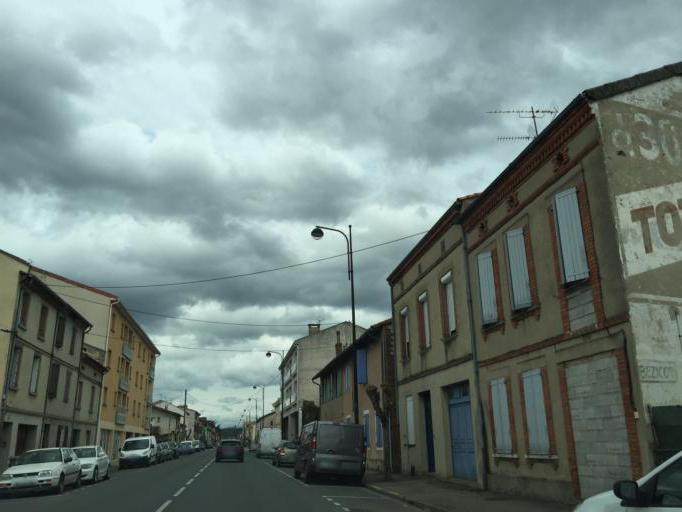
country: FR
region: Midi-Pyrenees
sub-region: Departement du Tarn
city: Albi
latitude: 43.9373
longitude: 2.1472
